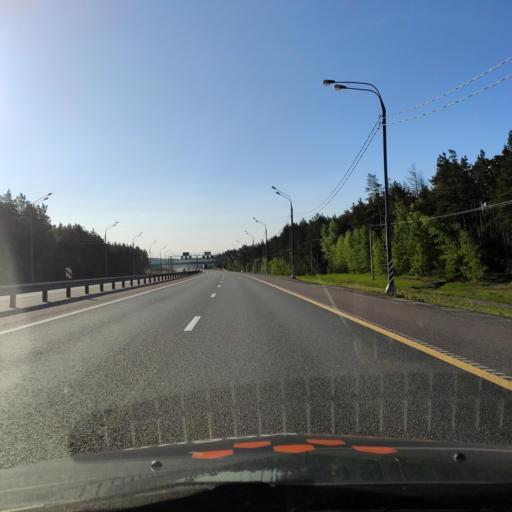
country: RU
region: Lipetsk
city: Zadonsk
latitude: 52.3791
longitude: 38.8825
